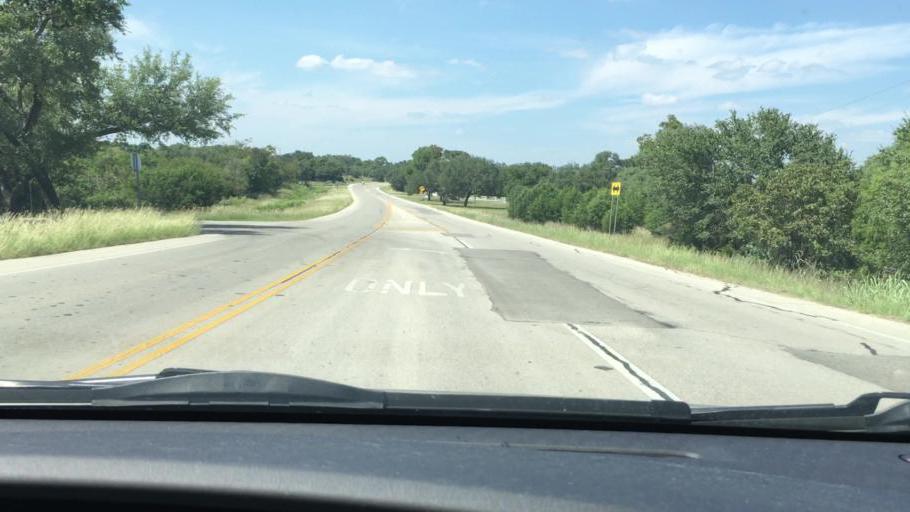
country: US
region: Texas
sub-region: Travis County
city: Shady Hollow
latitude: 30.1752
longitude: -97.9634
